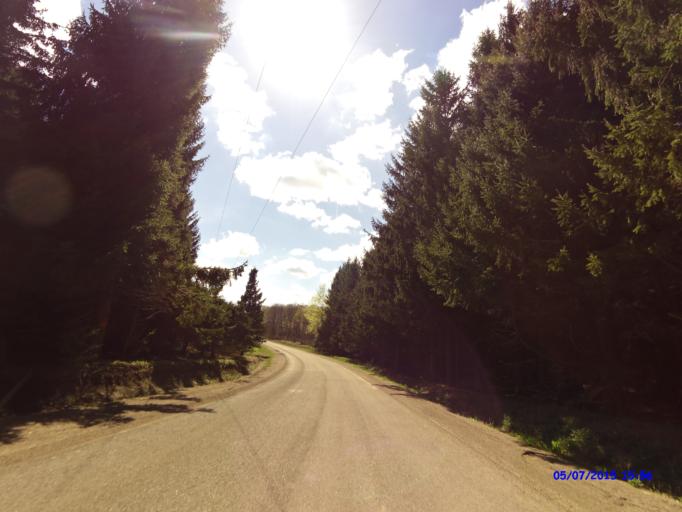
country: US
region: New York
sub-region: Cattaraugus County
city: Franklinville
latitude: 42.3161
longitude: -78.5635
